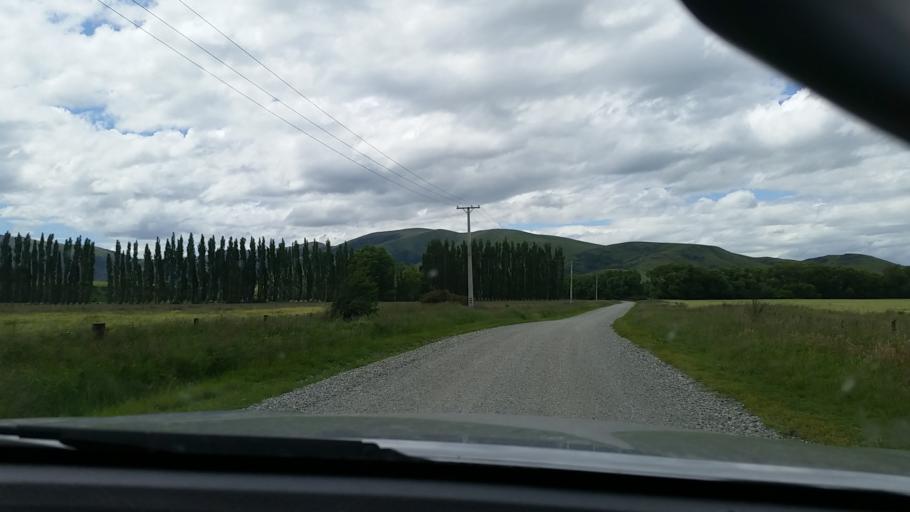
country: NZ
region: Otago
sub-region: Queenstown-Lakes District
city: Kingston
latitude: -45.7354
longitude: 168.6595
